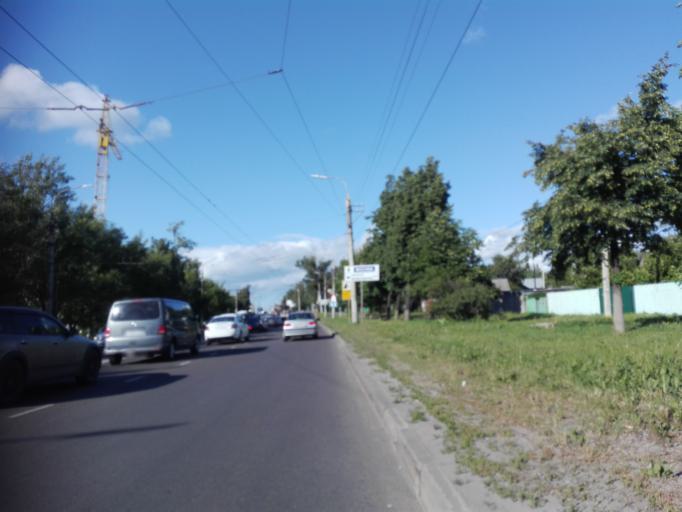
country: RU
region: Orjol
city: Orel
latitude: 52.9868
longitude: 36.1182
